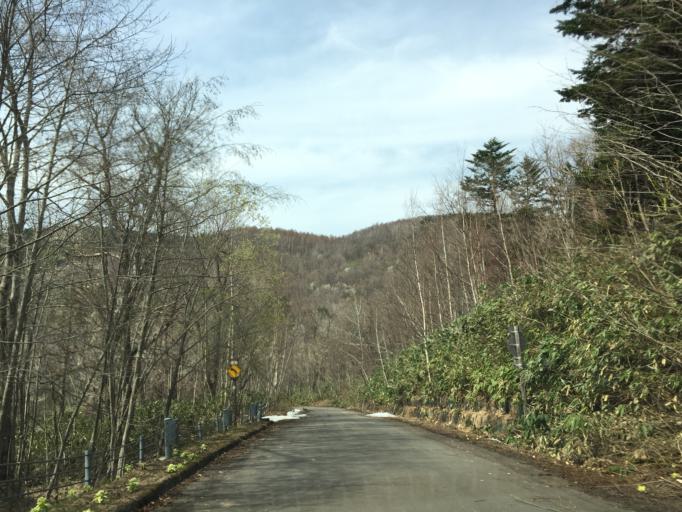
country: JP
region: Hokkaido
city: Akabira
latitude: 43.5996
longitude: 142.0605
